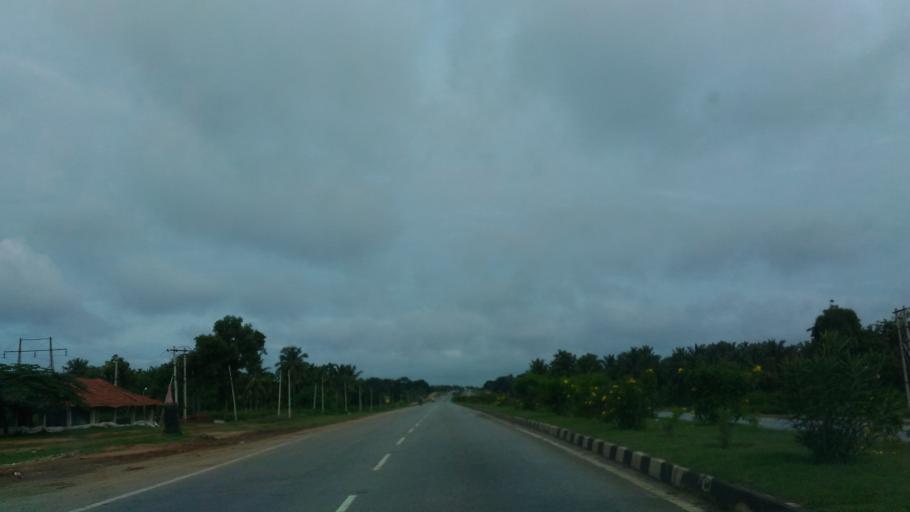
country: IN
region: Karnataka
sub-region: Tumkur
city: Kunigal
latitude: 13.0204
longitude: 77.0643
